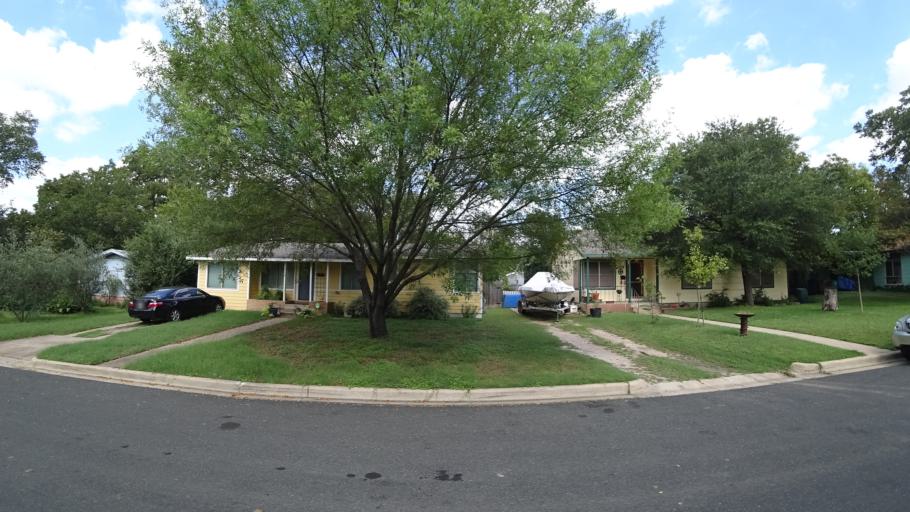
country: US
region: Texas
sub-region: Travis County
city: Austin
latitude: 30.3248
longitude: -97.7187
